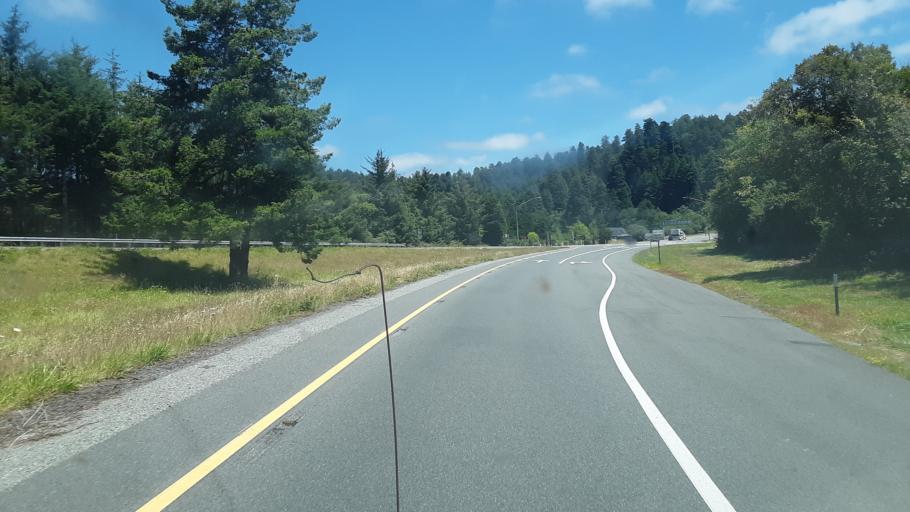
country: US
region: California
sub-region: Del Norte County
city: Bertsch-Oceanview
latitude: 41.8040
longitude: -124.1458
